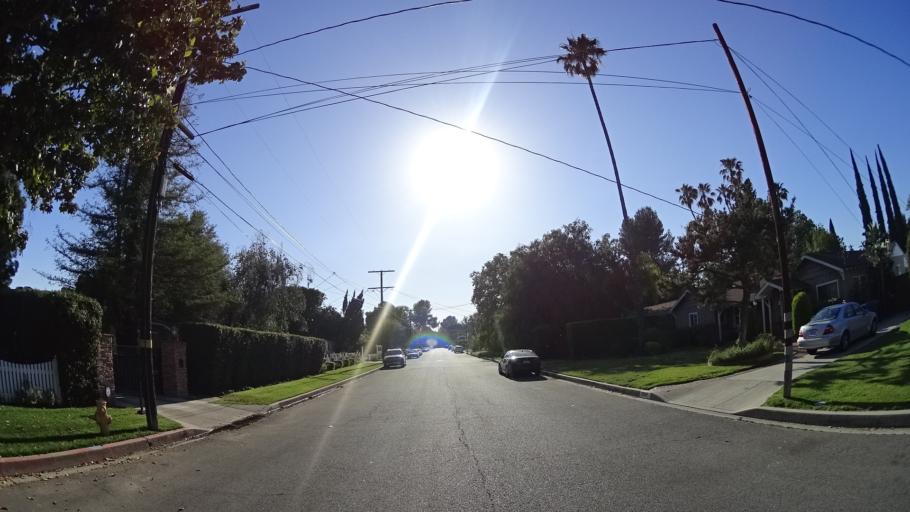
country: US
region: California
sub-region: Los Angeles County
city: North Hollywood
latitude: 34.1631
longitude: -118.4024
